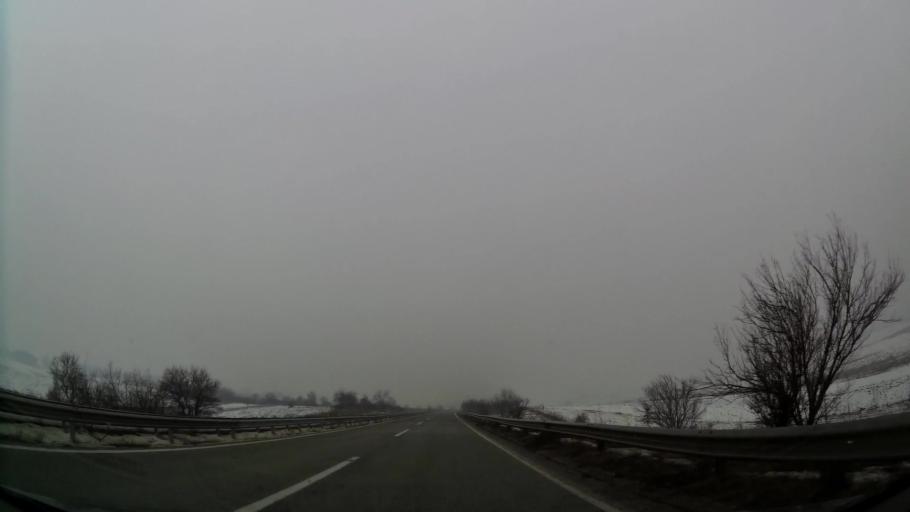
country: MK
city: Miladinovci
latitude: 41.9733
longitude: 21.6485
